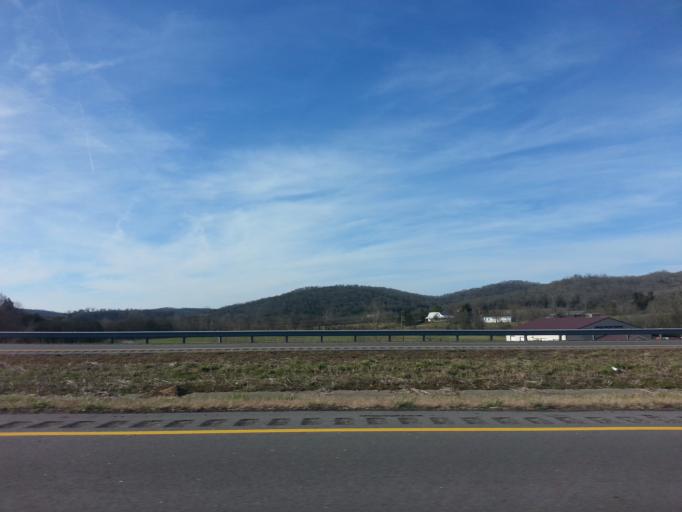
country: US
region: Tennessee
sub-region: Cannon County
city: Woodbury
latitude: 35.8120
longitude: -86.1227
